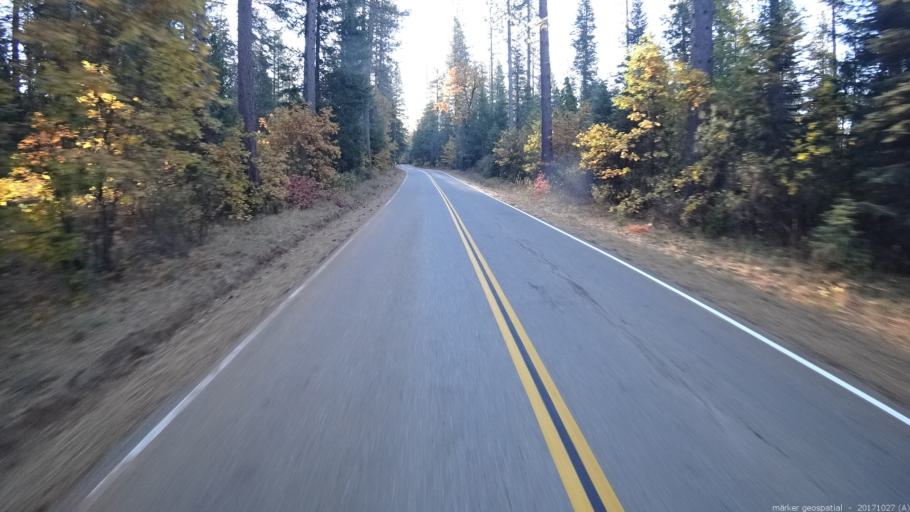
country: US
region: California
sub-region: Shasta County
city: Burney
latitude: 40.9317
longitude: -121.9445
